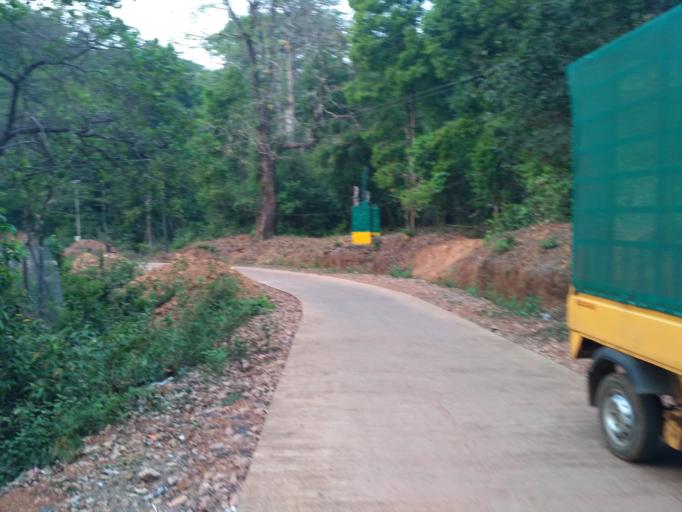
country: IN
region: Karnataka
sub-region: Kodagu
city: Somvarpet
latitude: 12.6613
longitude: 75.6204
